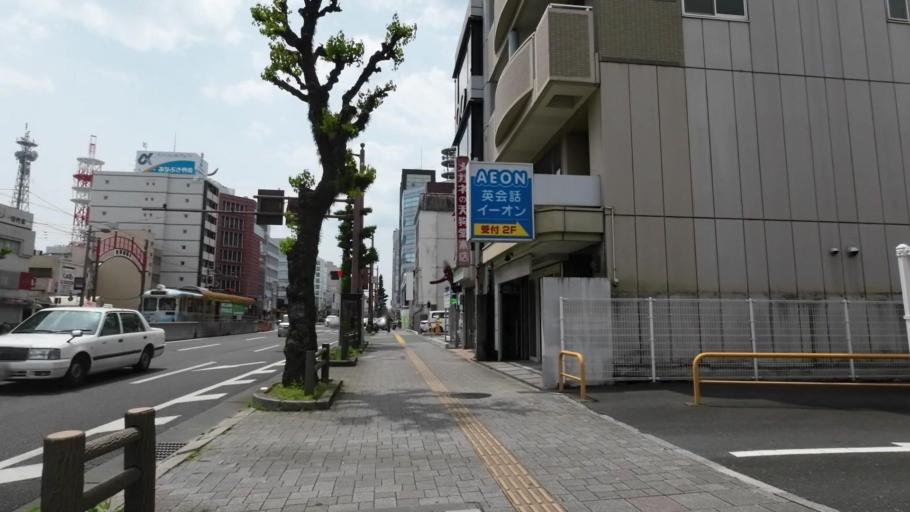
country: JP
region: Kochi
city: Kochi-shi
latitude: 33.5592
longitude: 133.5371
